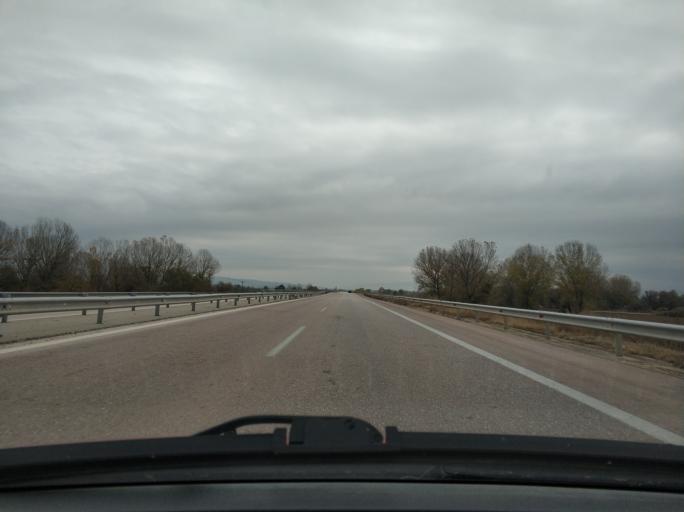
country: GR
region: Central Macedonia
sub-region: Nomos Thessalonikis
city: Kavallari
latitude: 40.7295
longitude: 23.0612
